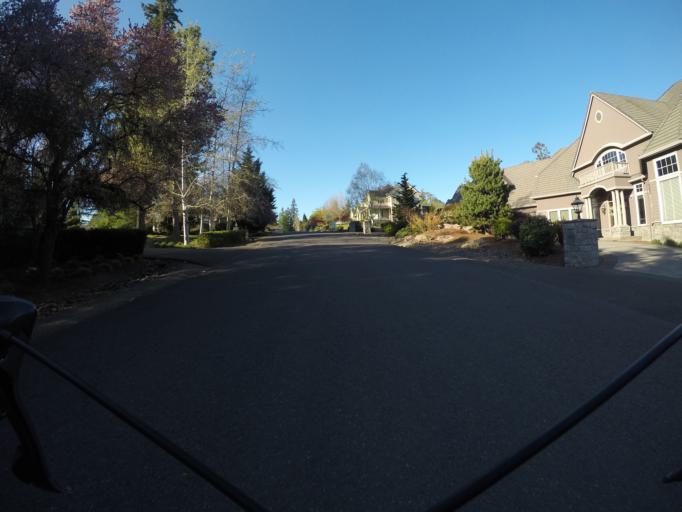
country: US
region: Oregon
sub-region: Washington County
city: Aloha
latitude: 45.4508
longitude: -122.8788
